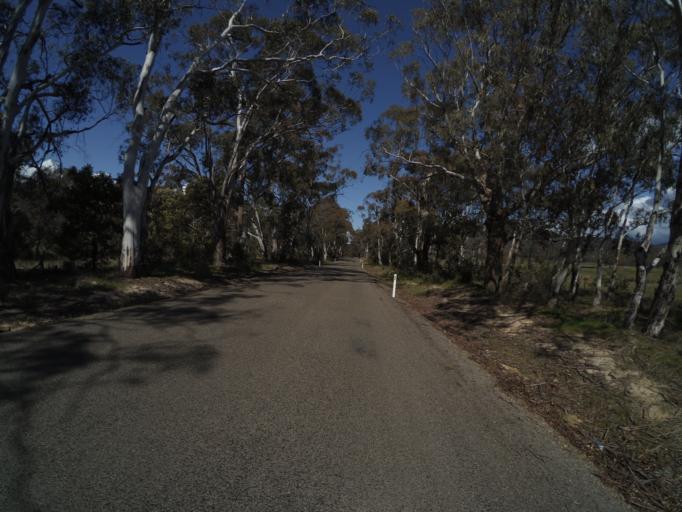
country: AU
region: Australian Capital Territory
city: Macquarie
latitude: -35.1939
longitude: 148.8902
